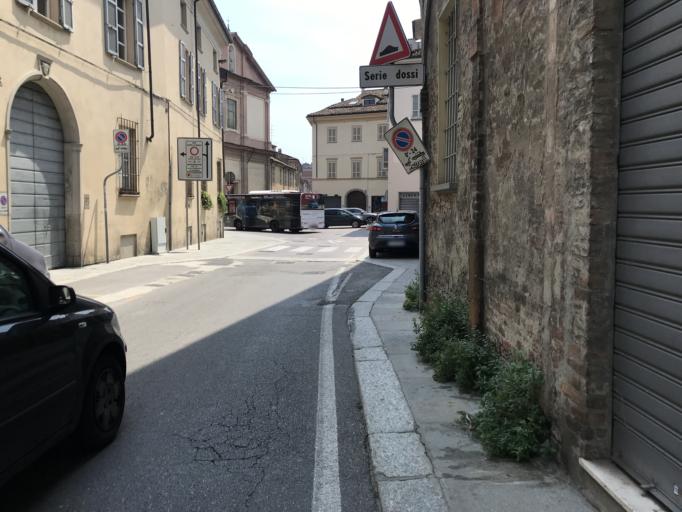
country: IT
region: Emilia-Romagna
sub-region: Provincia di Piacenza
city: Piacenza
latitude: 45.0488
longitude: 9.6996
